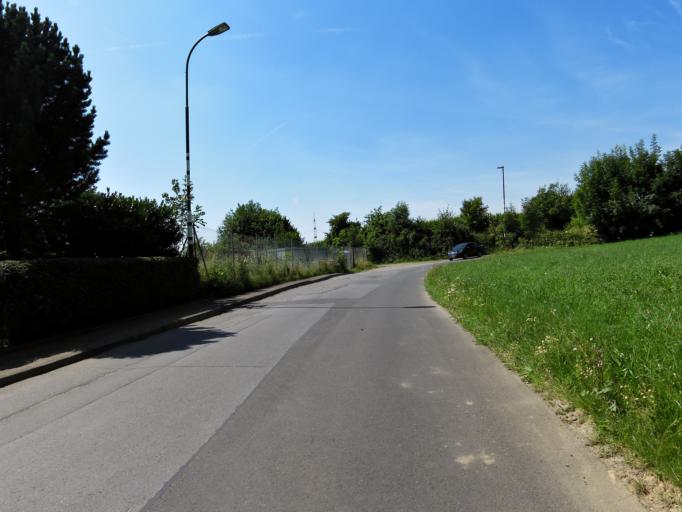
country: NL
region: Limburg
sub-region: Gemeente Kerkrade
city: Kerkrade
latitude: 50.8221
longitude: 6.0699
